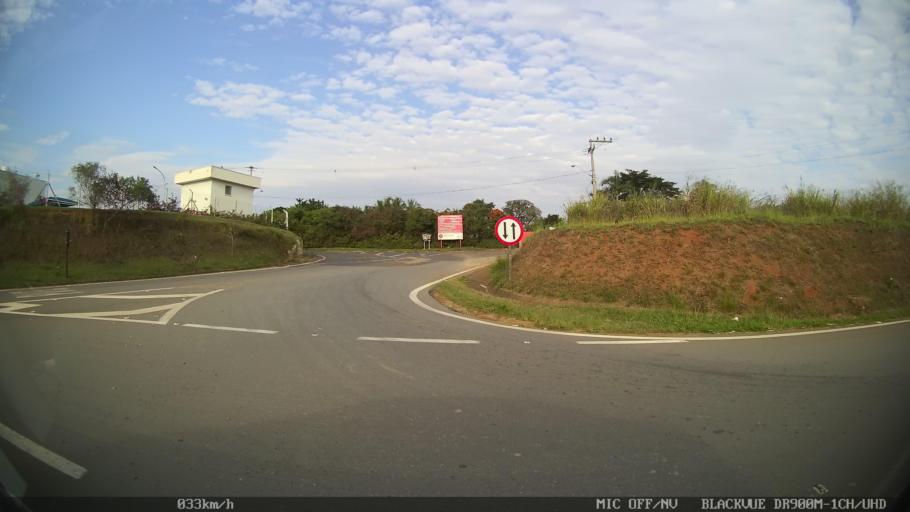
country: BR
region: Sao Paulo
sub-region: Artur Nogueira
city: Artur Nogueira
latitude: -22.5965
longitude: -47.1866
